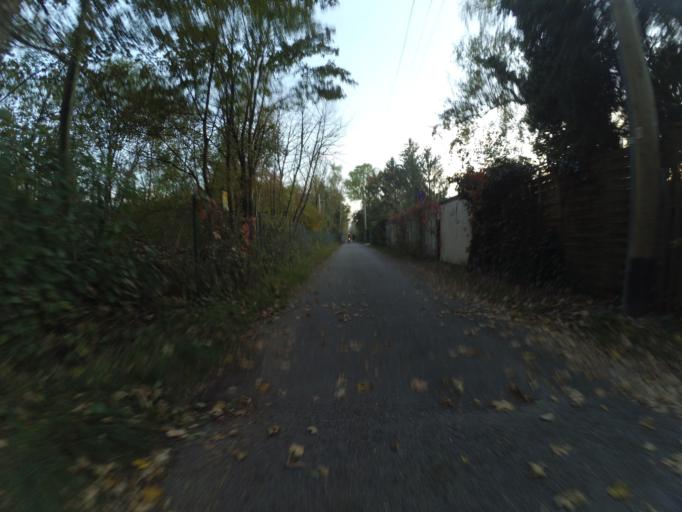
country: DE
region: Bavaria
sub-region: Upper Bavaria
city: Oberschleissheim
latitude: 48.1976
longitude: 11.5399
